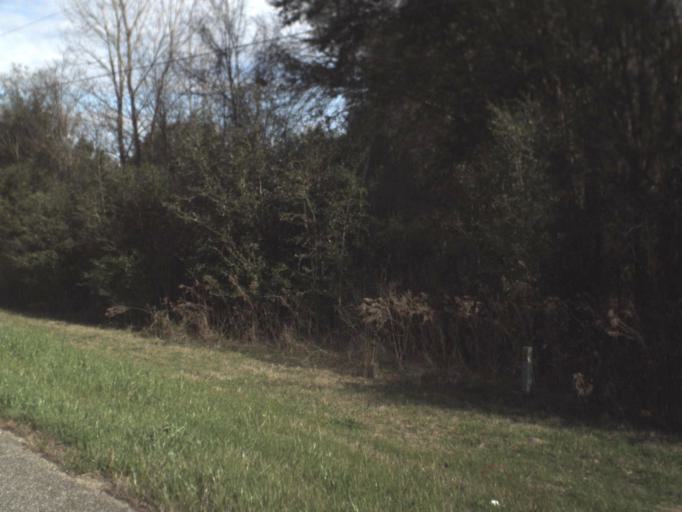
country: US
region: Florida
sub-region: Jackson County
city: Malone
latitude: 30.9918
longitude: -85.1933
